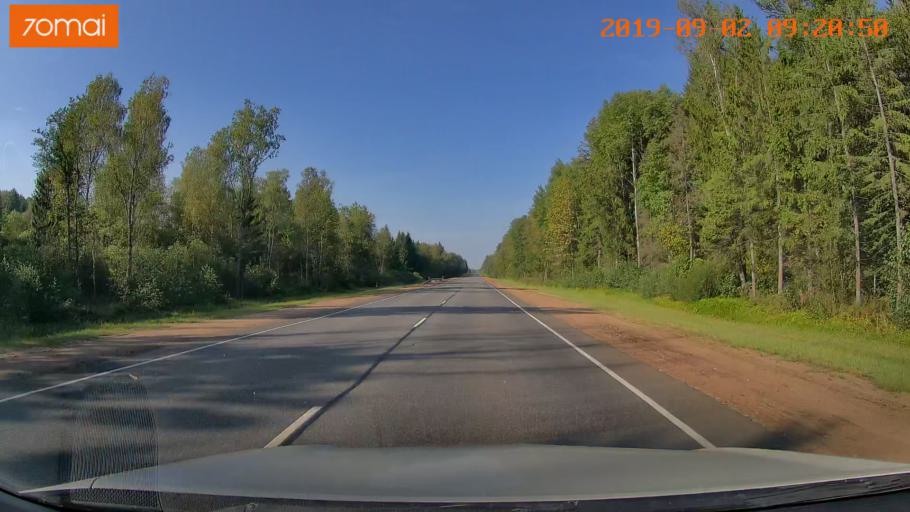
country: RU
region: Kaluga
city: Yukhnov
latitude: 54.7971
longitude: 35.3742
